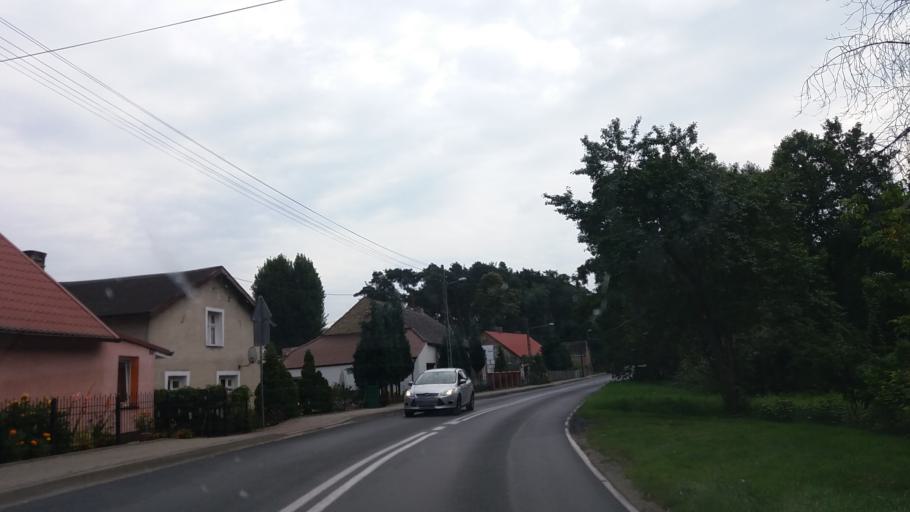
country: PL
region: Lubusz
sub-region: Powiat miedzyrzecki
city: Skwierzyna
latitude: 52.6414
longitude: 15.4519
